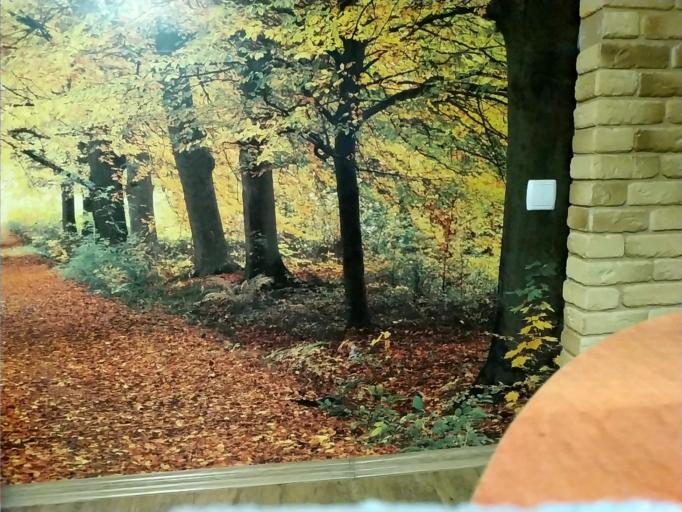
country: BY
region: Minsk
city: Plyeshchanitsy
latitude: 54.4272
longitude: 27.6011
